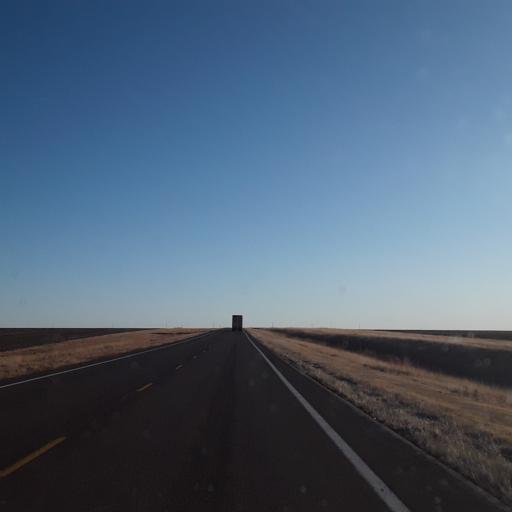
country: US
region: Kansas
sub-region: Sherman County
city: Goodland
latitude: 39.1441
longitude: -101.7268
